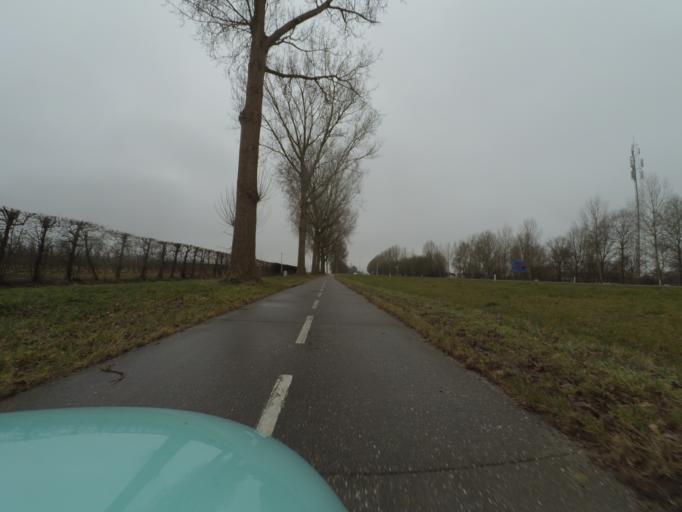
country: NL
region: Flevoland
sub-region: Gemeente Dronten
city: Dronten
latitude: 52.5160
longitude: 5.7331
